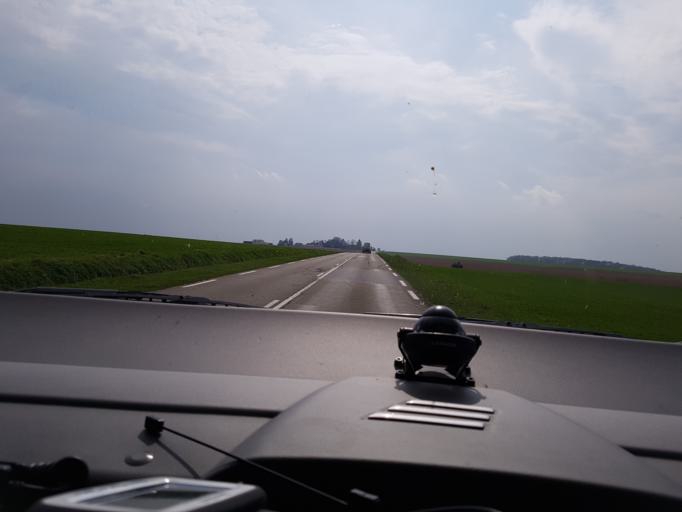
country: FR
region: Picardie
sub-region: Departement de l'Aisne
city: Crouy
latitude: 49.4546
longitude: 3.3543
